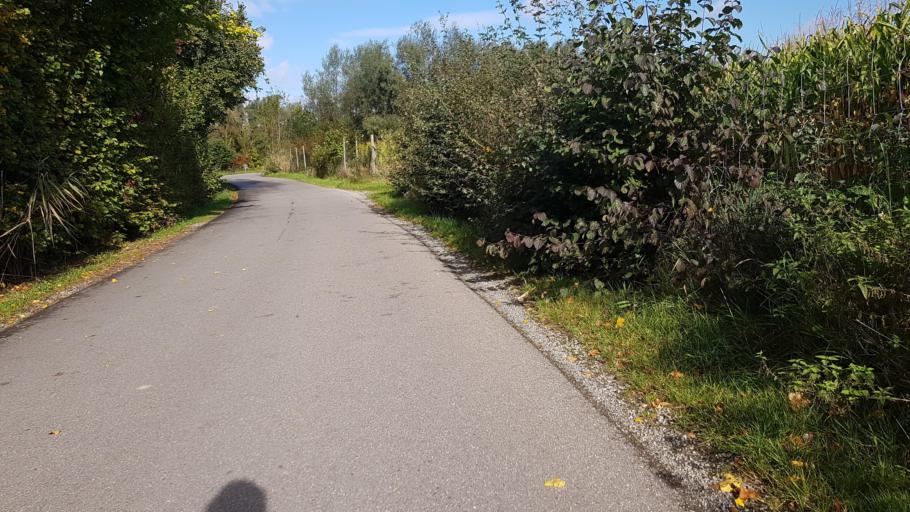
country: DE
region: Baden-Wuerttemberg
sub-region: Tuebingen Region
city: Eriskirch
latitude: 47.6238
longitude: 9.5322
